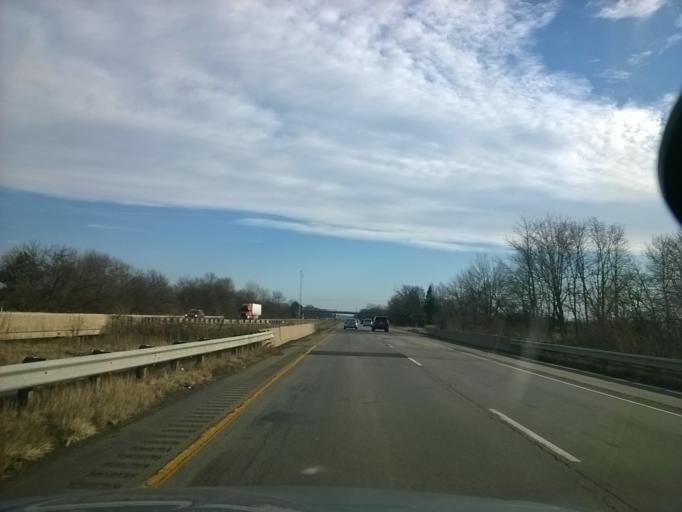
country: US
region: Indiana
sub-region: Johnson County
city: Franklin
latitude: 39.4458
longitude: -85.9912
